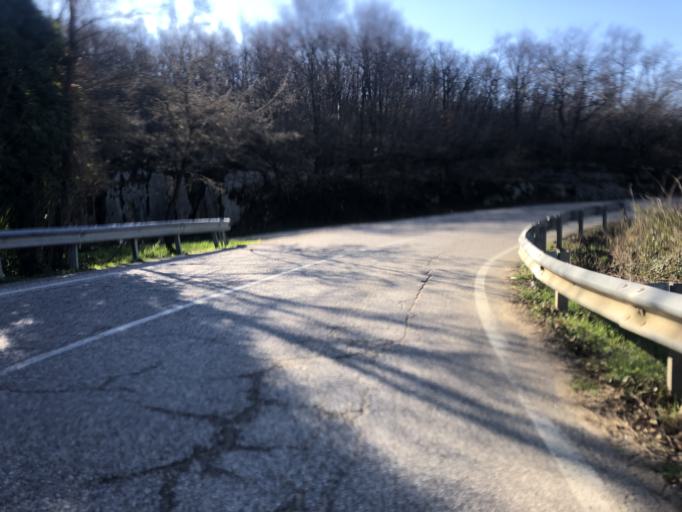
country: IT
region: Veneto
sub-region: Provincia di Verona
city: Volargne
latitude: 45.5488
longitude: 10.8420
